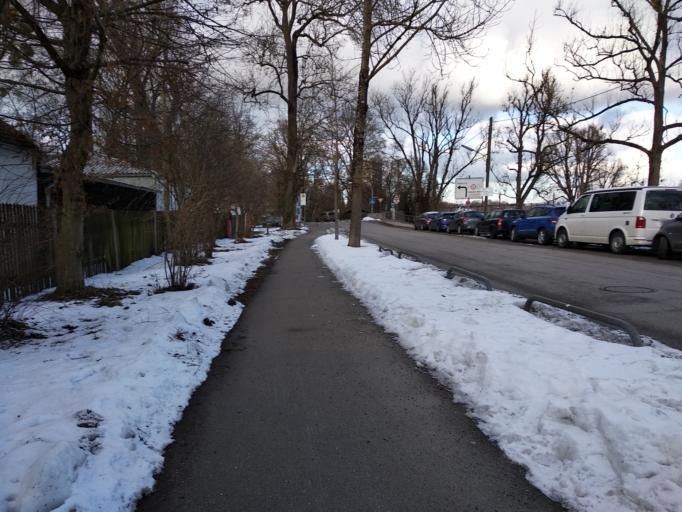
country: DE
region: Bavaria
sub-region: Upper Bavaria
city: Munich
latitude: 48.1001
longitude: 11.5481
